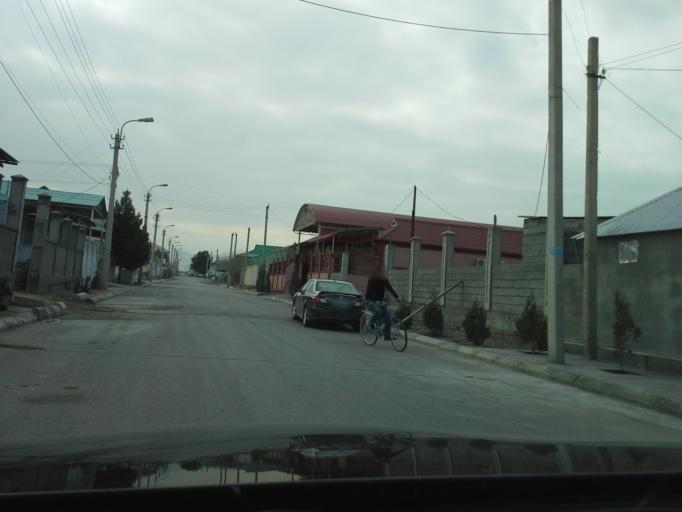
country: TM
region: Ahal
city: Abadan
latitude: 38.0420
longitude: 58.2711
